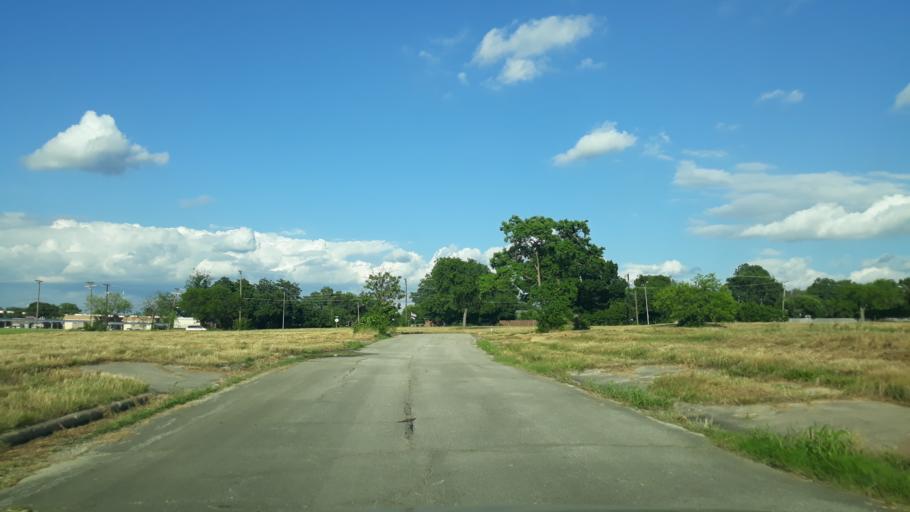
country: US
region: Texas
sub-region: Dallas County
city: Irving
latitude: 32.8537
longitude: -97.0097
